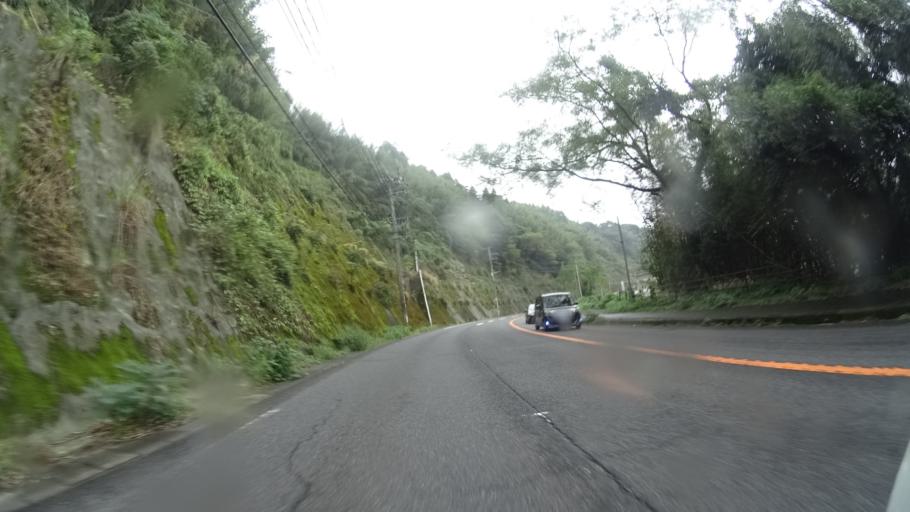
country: JP
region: Kagoshima
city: Kajiki
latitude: 31.7492
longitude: 130.6714
